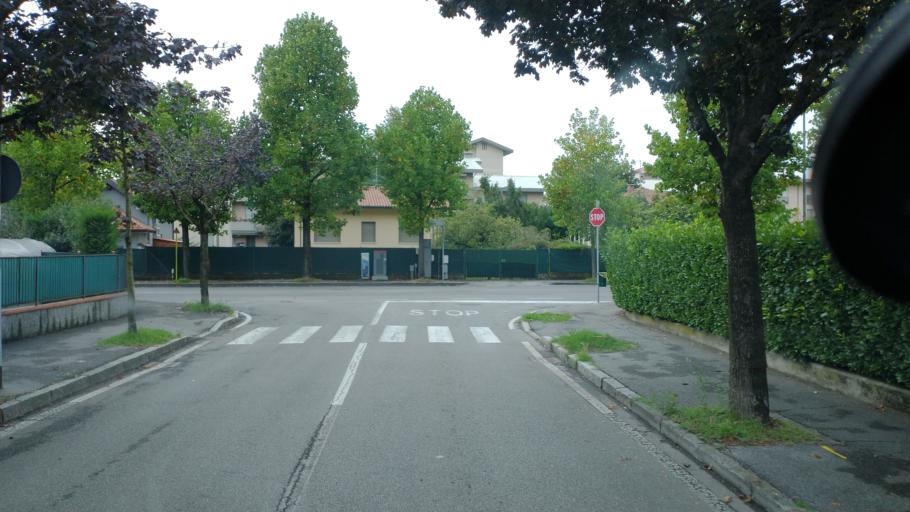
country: IT
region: Lombardy
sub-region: Provincia di Bergamo
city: Treviglio
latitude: 45.5333
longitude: 9.5937
